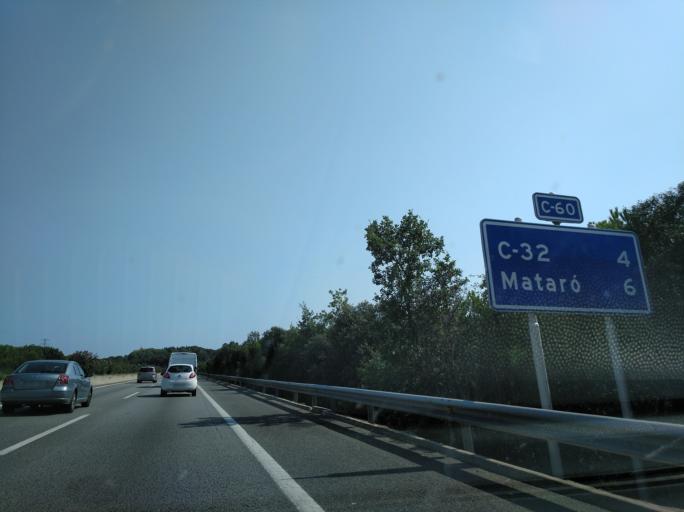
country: ES
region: Catalonia
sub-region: Provincia de Barcelona
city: Argentona
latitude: 41.5660
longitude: 2.3971
